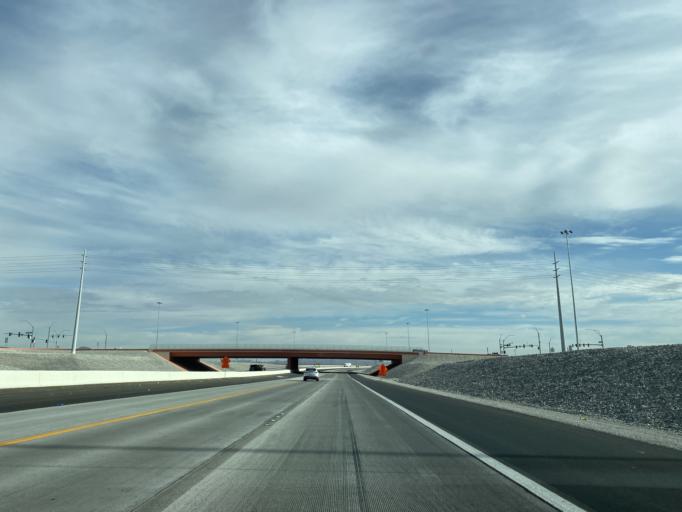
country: US
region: Nevada
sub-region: Clark County
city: Nellis Air Force Base
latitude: 36.2898
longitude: -115.0826
